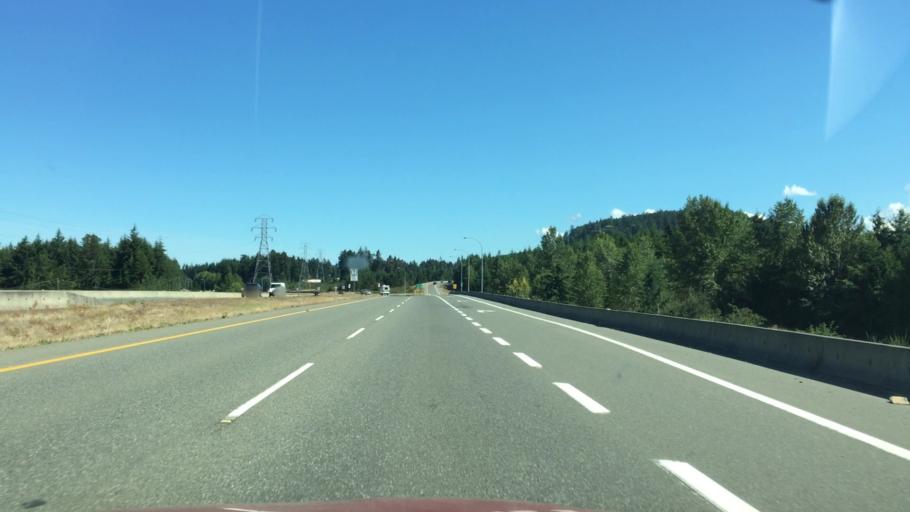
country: CA
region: British Columbia
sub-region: Regional District of Nanaimo
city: Parksville
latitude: 49.3088
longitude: -124.3396
